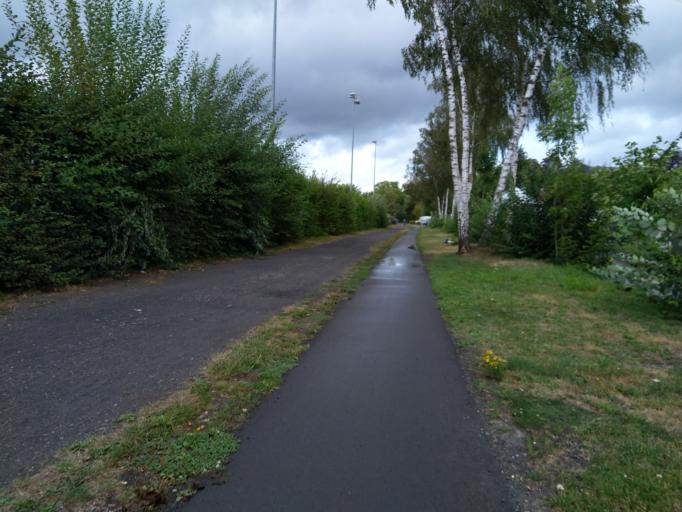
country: BE
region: Wallonia
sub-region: Province de Liege
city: Aubel
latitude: 50.7038
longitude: 5.8632
